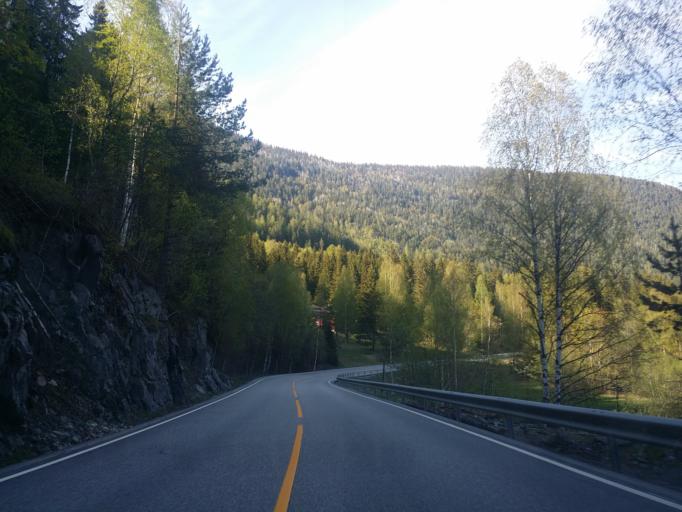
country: NO
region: Telemark
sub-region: Hjartdal
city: Sauland
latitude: 59.6145
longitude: 8.7894
